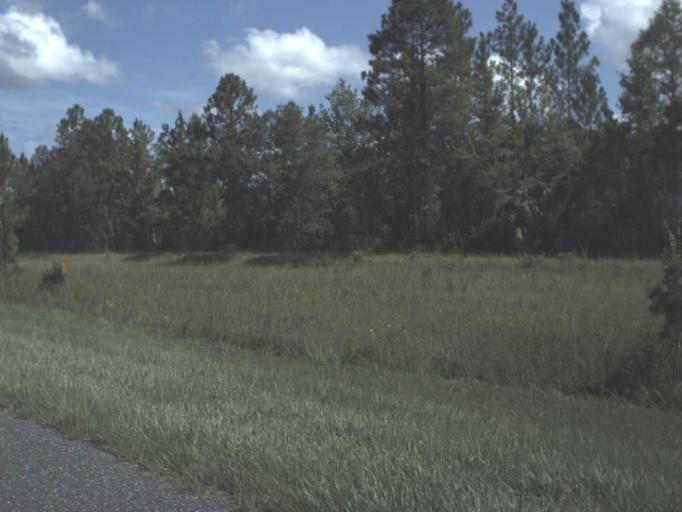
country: US
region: Florida
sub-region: Levy County
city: Bronson
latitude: 29.3040
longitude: -82.7541
